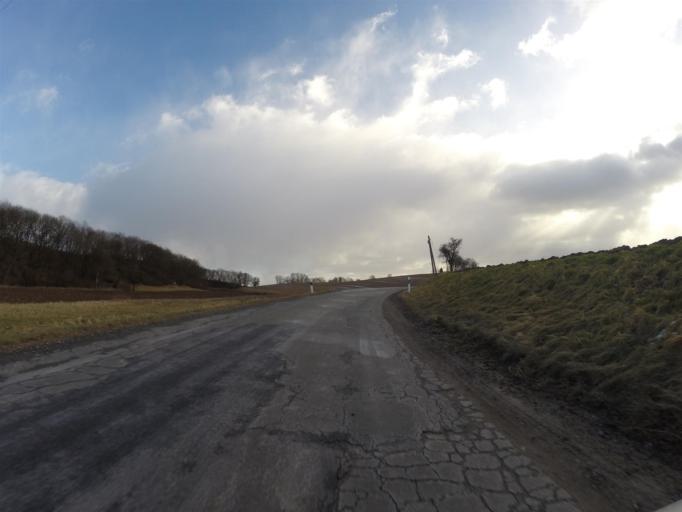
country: DE
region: Thuringia
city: Jenalobnitz
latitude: 50.9410
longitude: 11.7158
